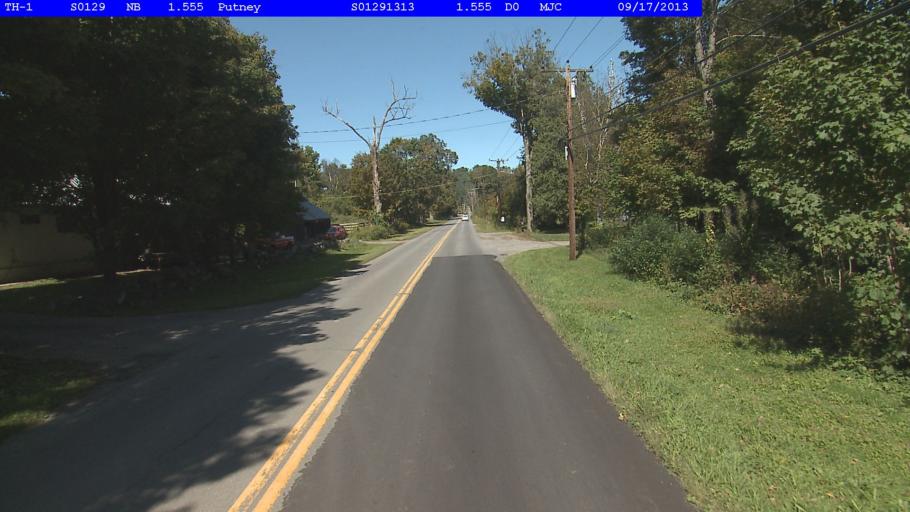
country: US
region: New Hampshire
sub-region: Cheshire County
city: Westmoreland
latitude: 42.9950
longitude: -72.5321
